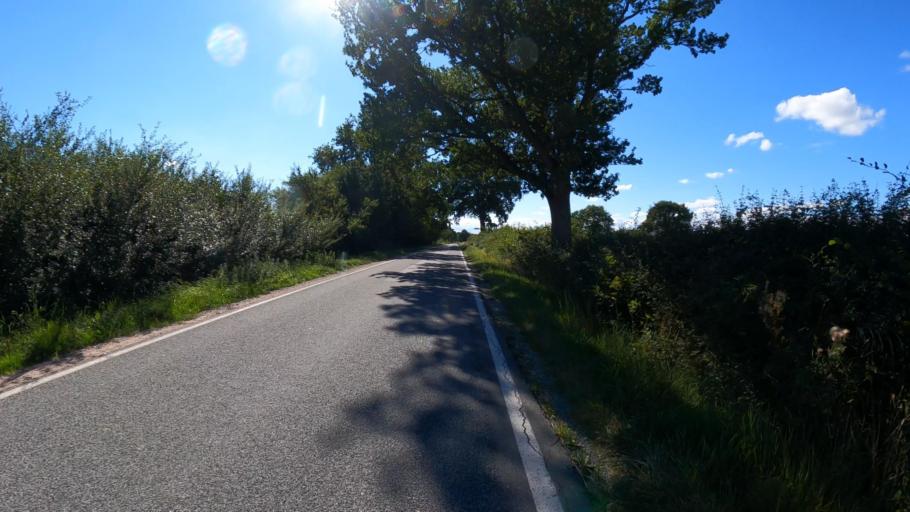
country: DE
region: Schleswig-Holstein
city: Grinau
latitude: 53.7971
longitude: 10.5484
